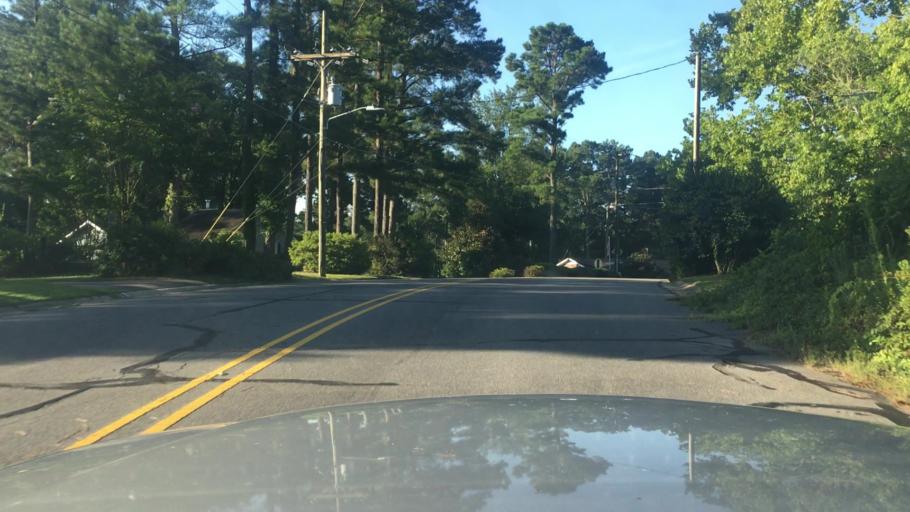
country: US
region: North Carolina
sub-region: Cumberland County
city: Fayetteville
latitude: 35.1184
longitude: -78.8717
